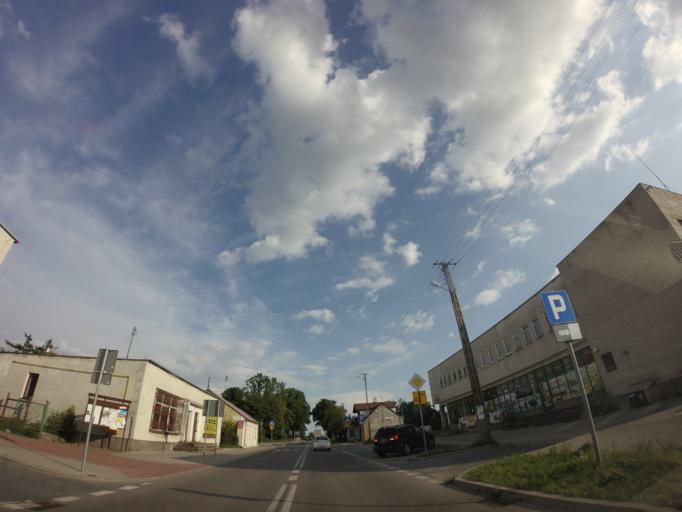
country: PL
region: Lublin Voivodeship
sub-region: Powiat lubartowski
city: Jeziorzany
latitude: 51.6012
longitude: 22.2771
